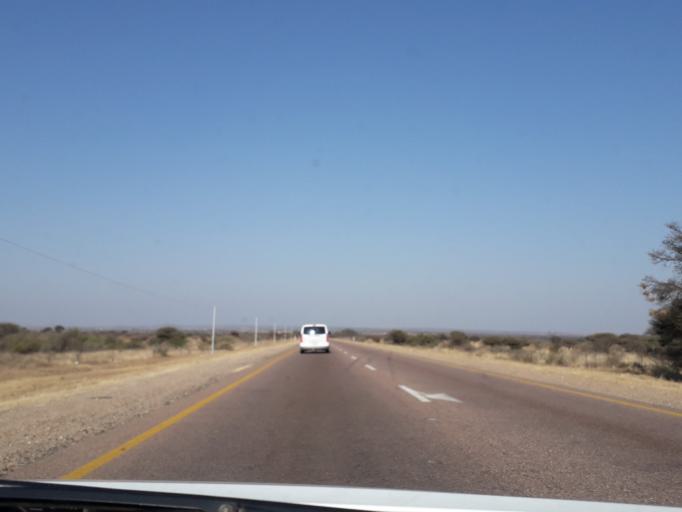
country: ZA
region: Limpopo
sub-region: Capricorn District Municipality
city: Mankoeng
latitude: -23.7597
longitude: 29.6678
